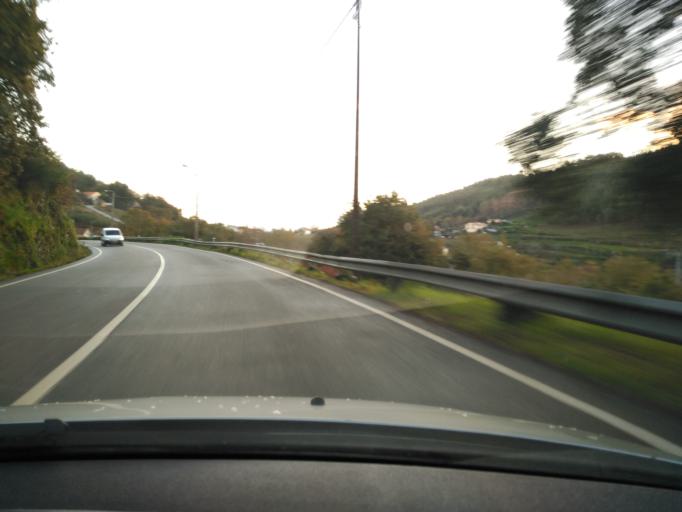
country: PT
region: Braga
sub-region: Braga
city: Braga
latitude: 41.5017
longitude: -8.3961
